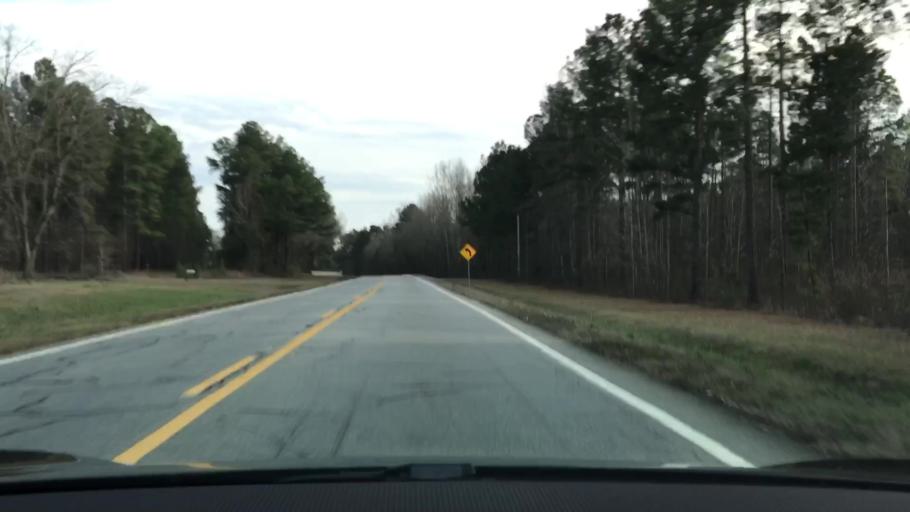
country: US
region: Georgia
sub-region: Warren County
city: Warrenton
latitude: 33.3503
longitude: -82.5851
